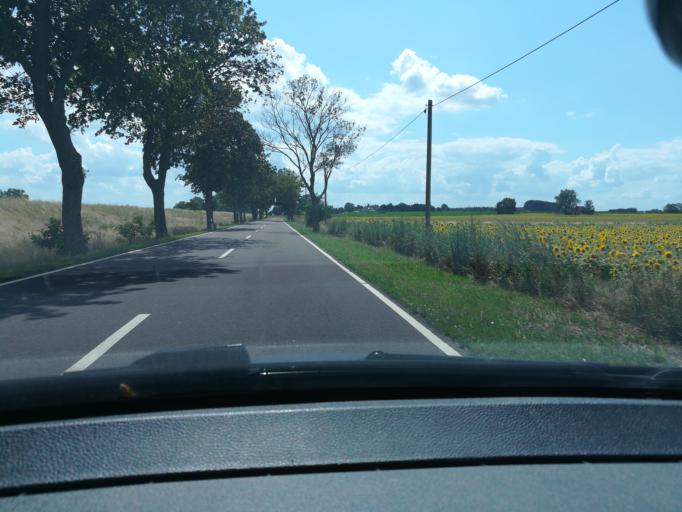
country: DE
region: Saxony-Anhalt
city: Rogatz
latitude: 52.3371
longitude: 11.7800
